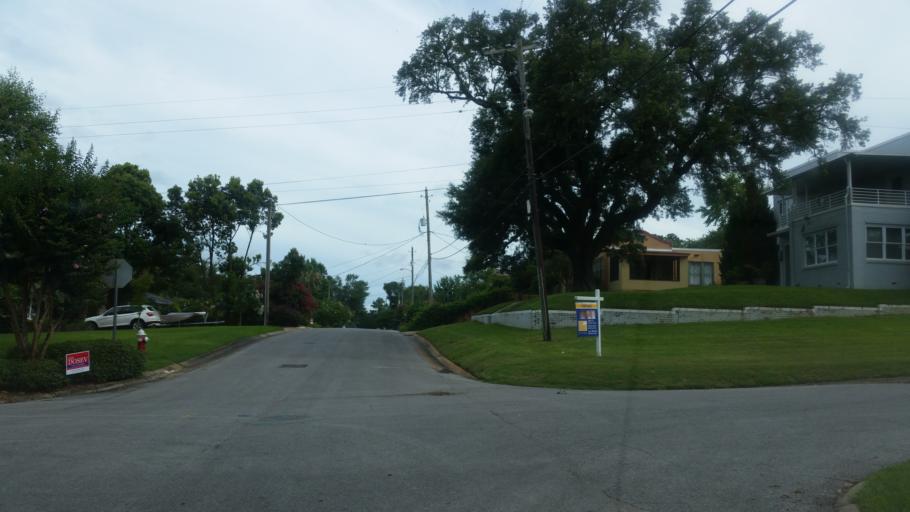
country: US
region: Florida
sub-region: Escambia County
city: East Pensacola Heights
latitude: 30.4369
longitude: -87.1899
